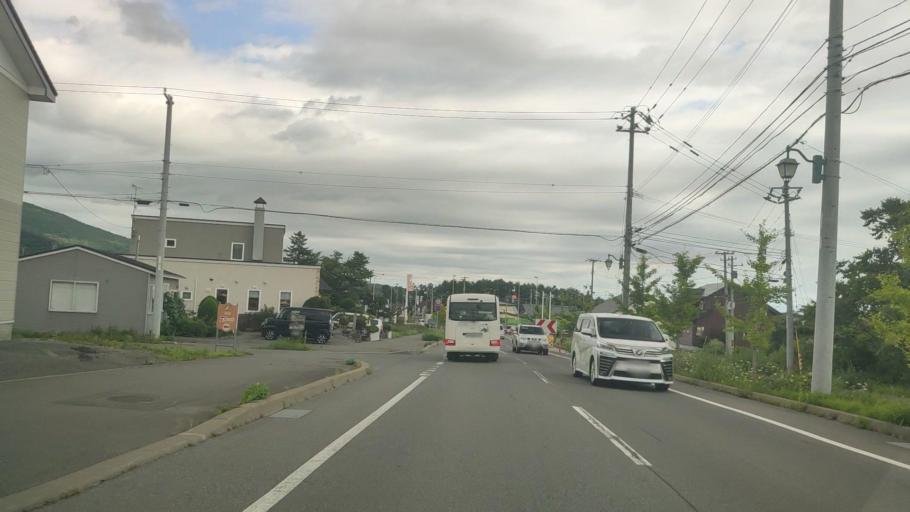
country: JP
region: Hokkaido
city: Date
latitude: 42.5498
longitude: 140.7702
